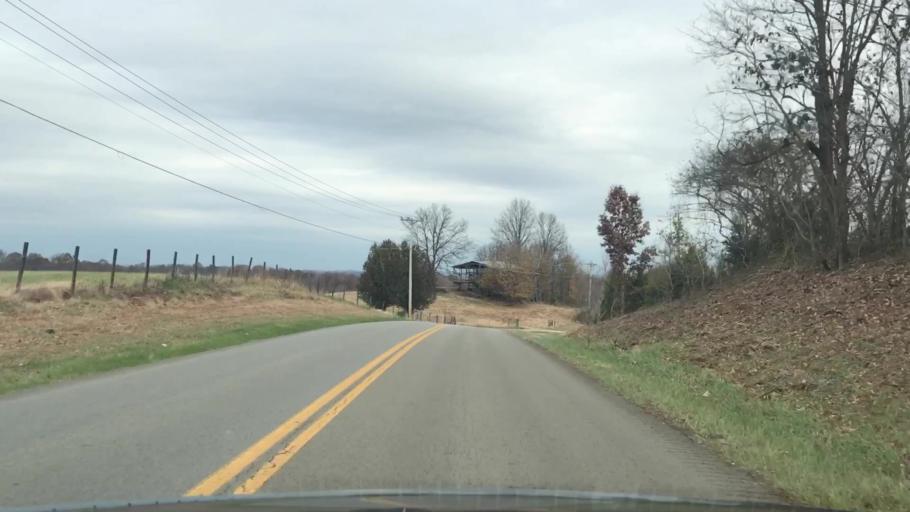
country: US
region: Kentucky
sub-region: Metcalfe County
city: Edmonton
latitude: 36.9164
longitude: -85.6489
